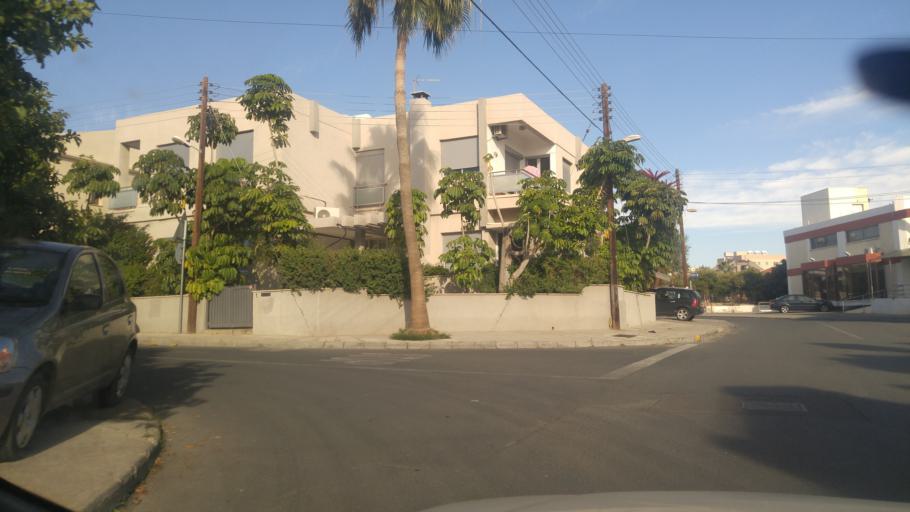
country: CY
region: Limassol
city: Limassol
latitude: 34.7020
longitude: 33.0440
